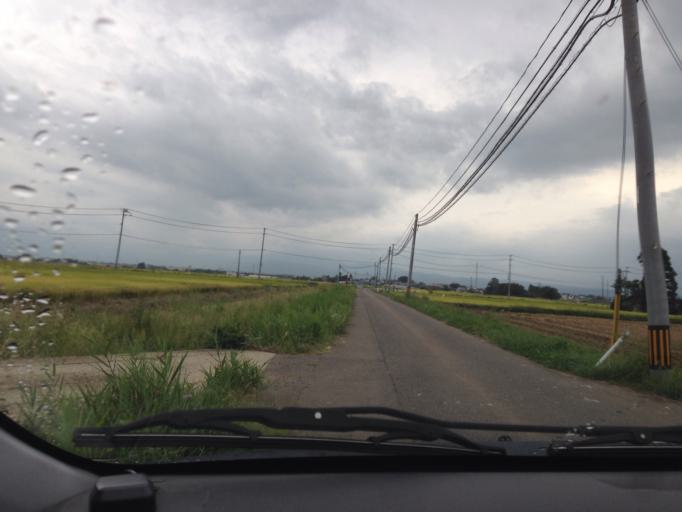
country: JP
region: Fukushima
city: Kitakata
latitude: 37.6029
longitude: 139.9034
